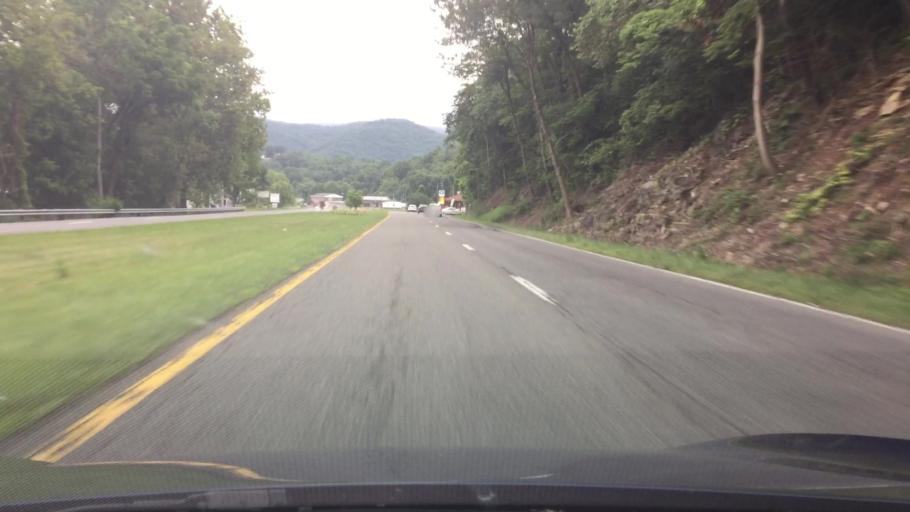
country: US
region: Virginia
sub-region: Montgomery County
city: Shawsville
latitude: 37.1700
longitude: -80.2633
